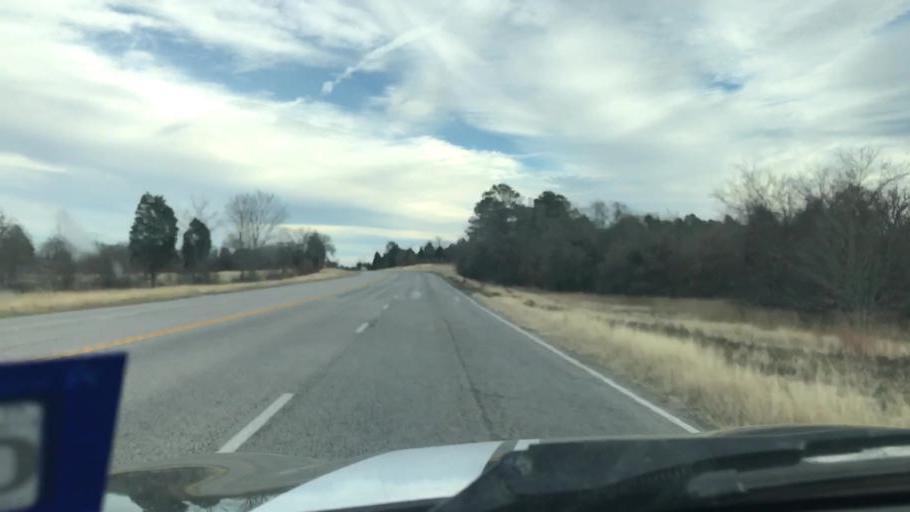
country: US
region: Texas
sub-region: Bastrop County
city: Elgin
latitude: 30.2999
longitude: -97.2894
